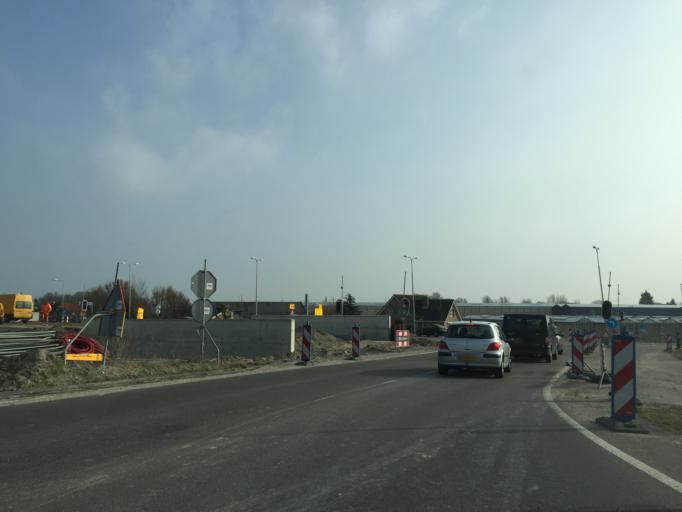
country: NL
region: South Holland
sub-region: Gemeente Westland
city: Maasdijk
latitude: 51.9705
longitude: 4.2031
